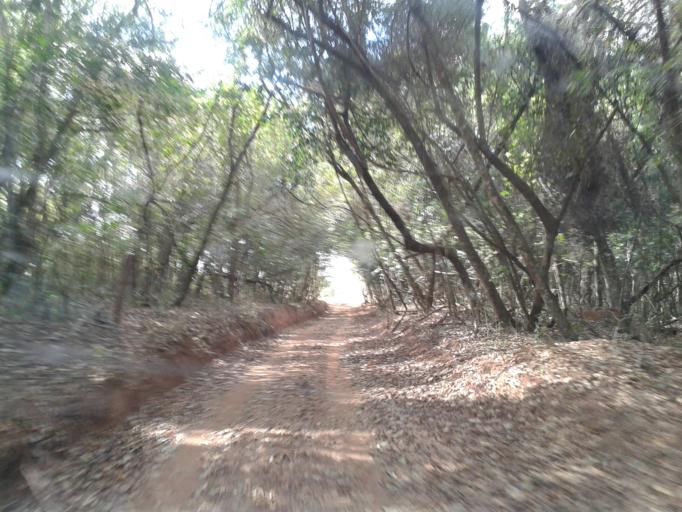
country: BR
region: Minas Gerais
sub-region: Monte Alegre De Minas
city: Monte Alegre de Minas
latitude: -18.7930
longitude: -49.0945
